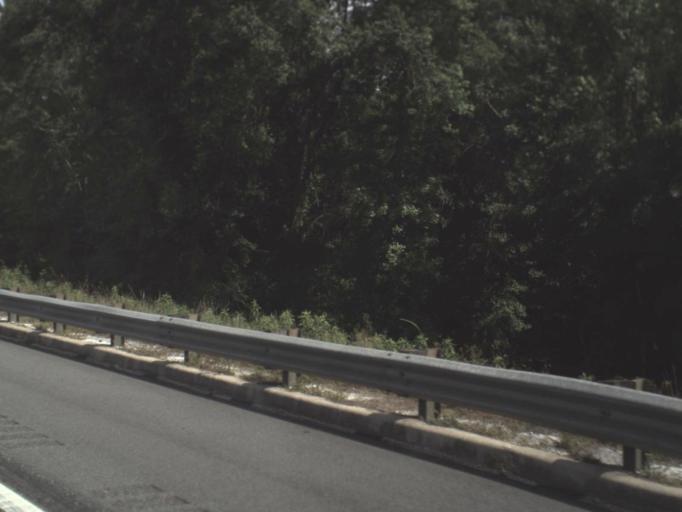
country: US
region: Florida
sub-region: Suwannee County
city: Wellborn
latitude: 30.2675
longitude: -82.7584
